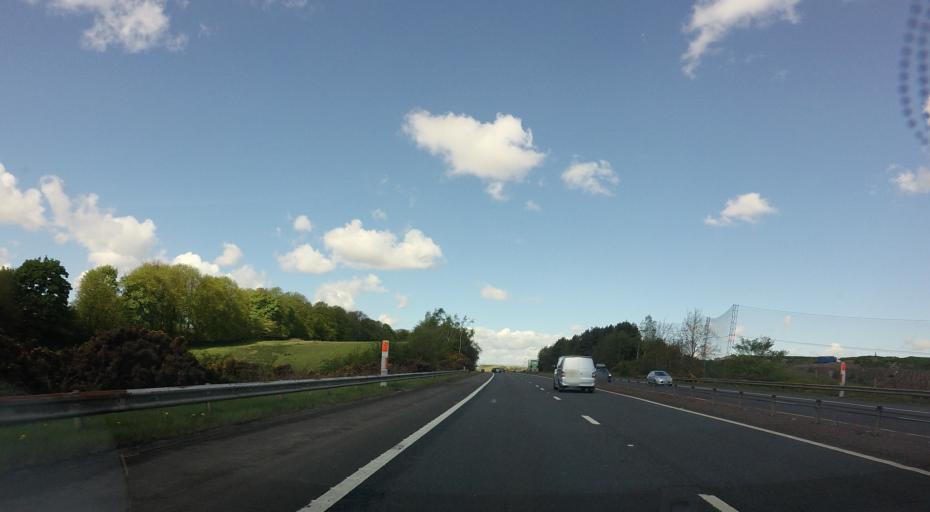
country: GB
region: Scotland
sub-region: Falkirk
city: Polmont
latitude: 55.9871
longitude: -3.6667
